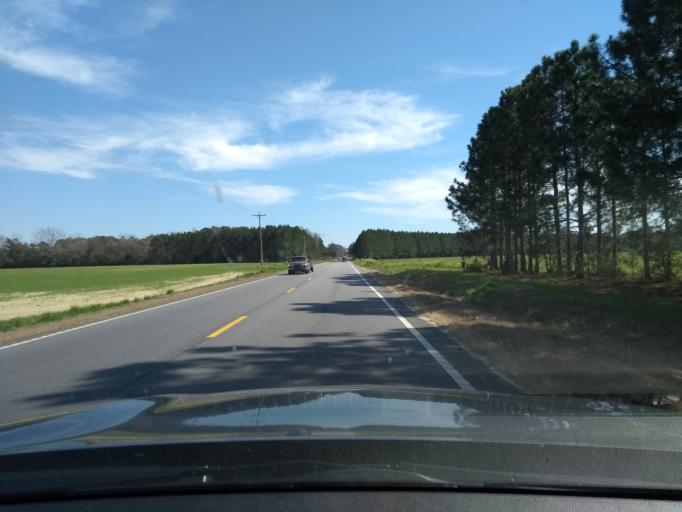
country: US
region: Georgia
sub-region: Bulloch County
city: Brooklet
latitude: 32.4762
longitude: -81.6105
